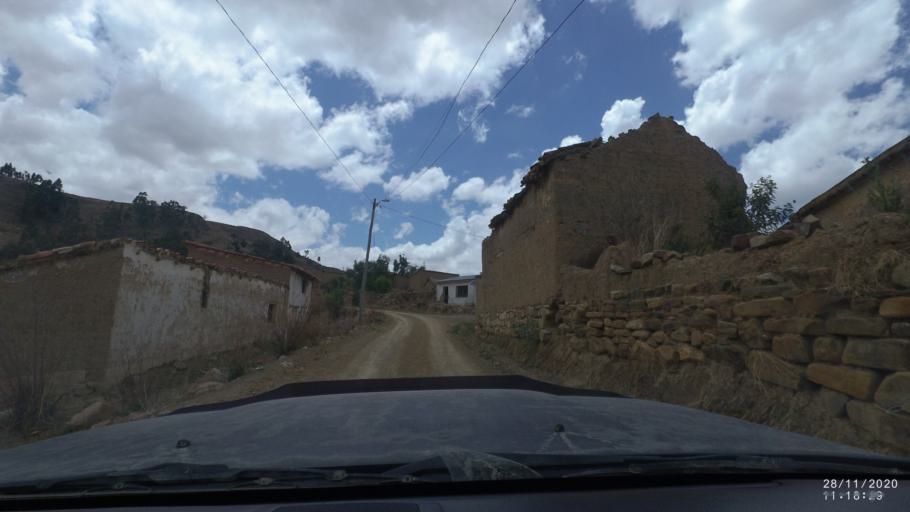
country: BO
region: Cochabamba
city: Tarata
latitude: -17.7535
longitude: -66.0736
